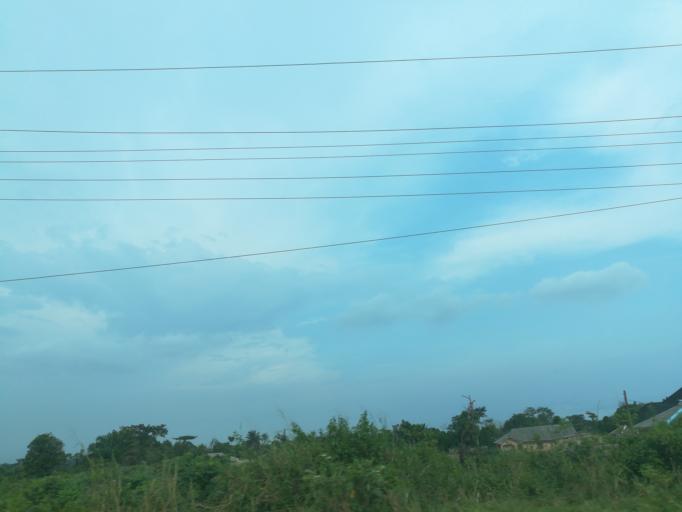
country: NG
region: Lagos
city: Ikorodu
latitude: 6.6415
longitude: 3.6706
